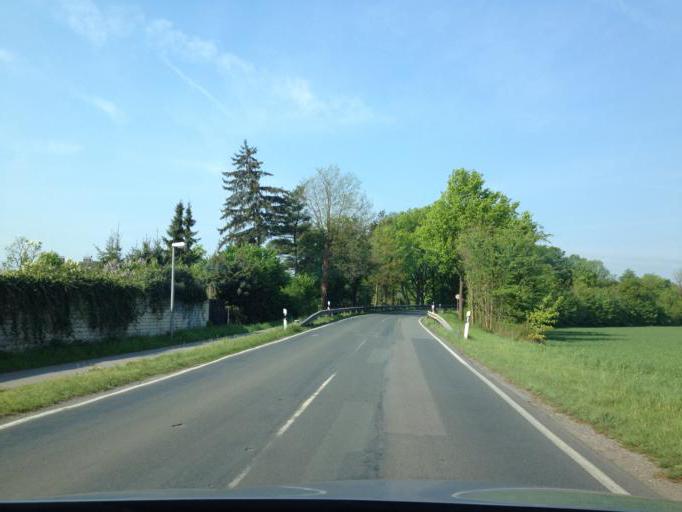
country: DE
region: North Rhine-Westphalia
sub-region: Regierungsbezirk Detmold
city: Verl
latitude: 51.8945
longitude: 8.4583
